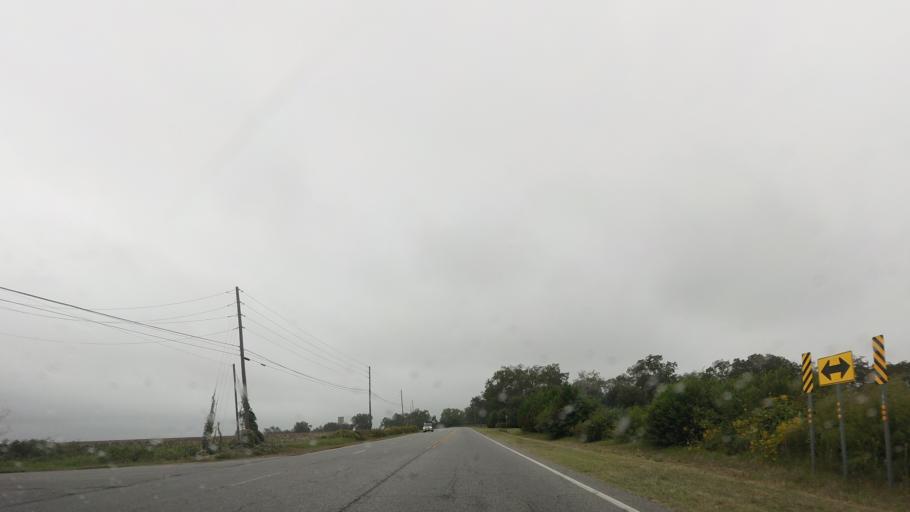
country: US
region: Georgia
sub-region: Ben Hill County
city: Fitzgerald
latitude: 31.6793
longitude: -83.2369
